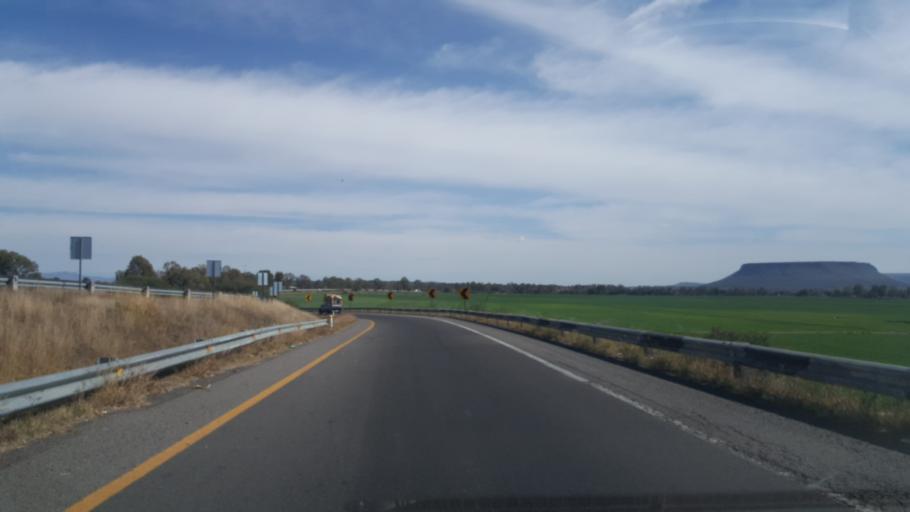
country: MX
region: Jalisco
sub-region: Lagos de Moreno
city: Cristeros [Fraccionamiento]
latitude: 21.3164
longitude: -102.0464
